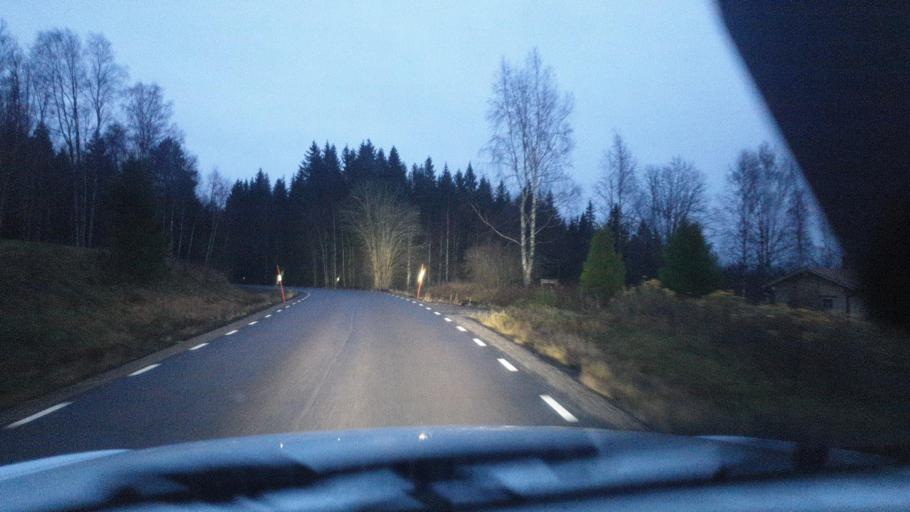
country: SE
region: Vaermland
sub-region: Torsby Kommun
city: Torsby
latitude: 59.9859
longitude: 12.7593
